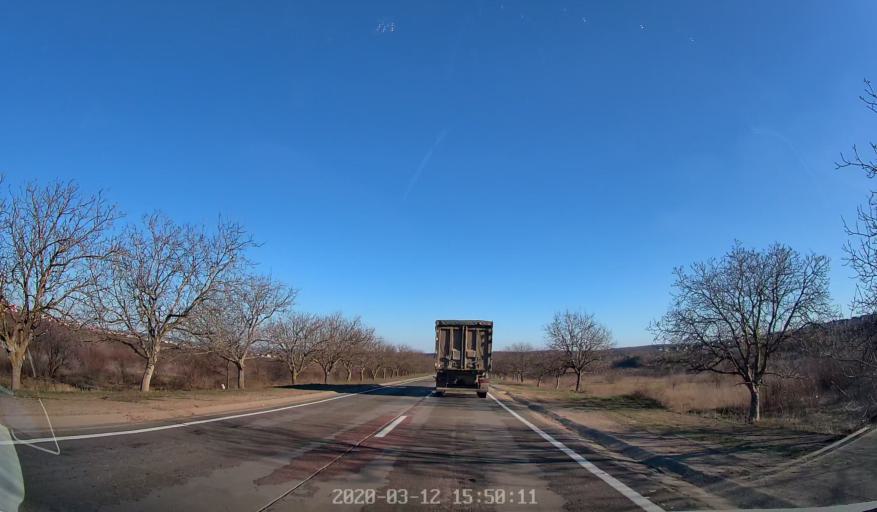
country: MD
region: Chisinau
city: Ciorescu
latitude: 47.0754
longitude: 28.9519
